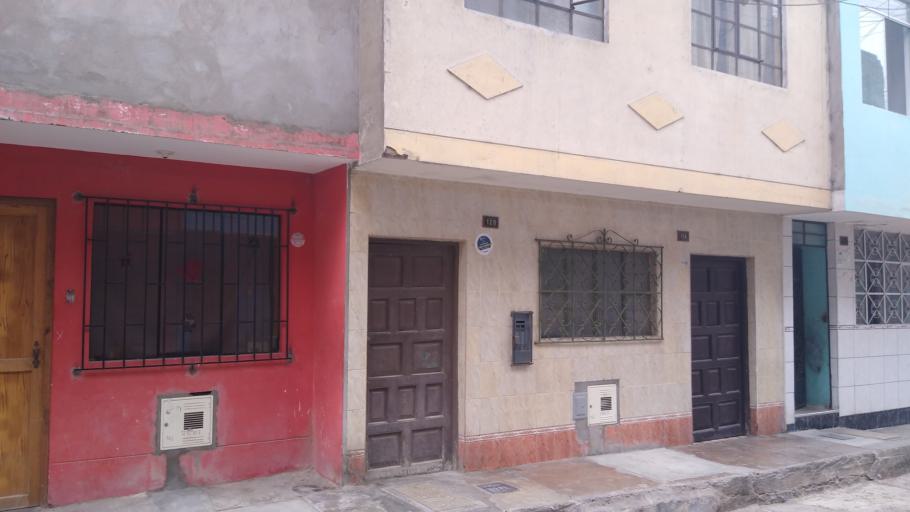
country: PE
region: Callao
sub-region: Callao
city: Callao
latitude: -12.0436
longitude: -77.0942
